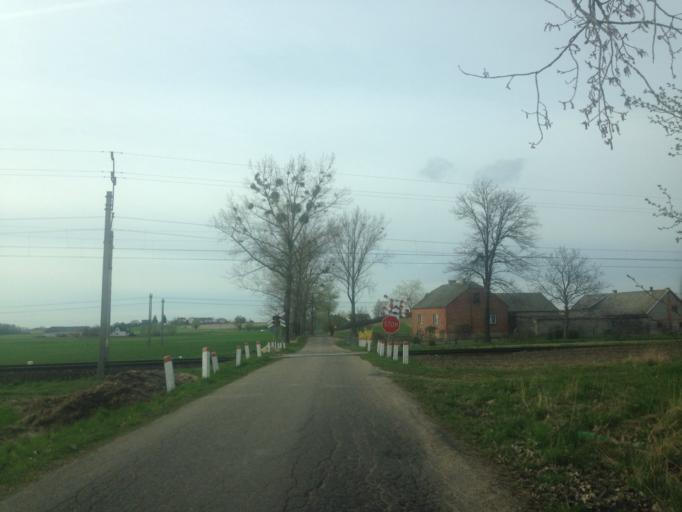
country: PL
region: Kujawsko-Pomorskie
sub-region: Powiat brodnicki
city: Jablonowo Pomorskie
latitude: 53.4057
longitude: 19.2211
